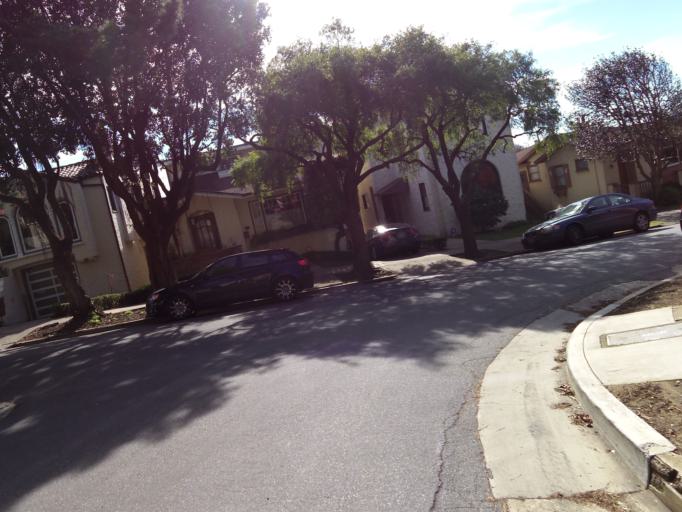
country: US
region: California
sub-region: San Mateo County
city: Daly City
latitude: 37.7452
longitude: -122.4652
